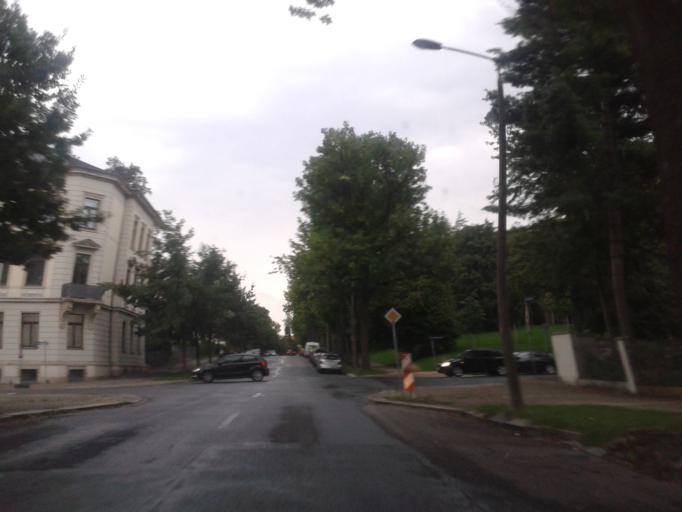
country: DE
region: Saxony
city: Dresden
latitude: 51.0323
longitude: 13.7415
